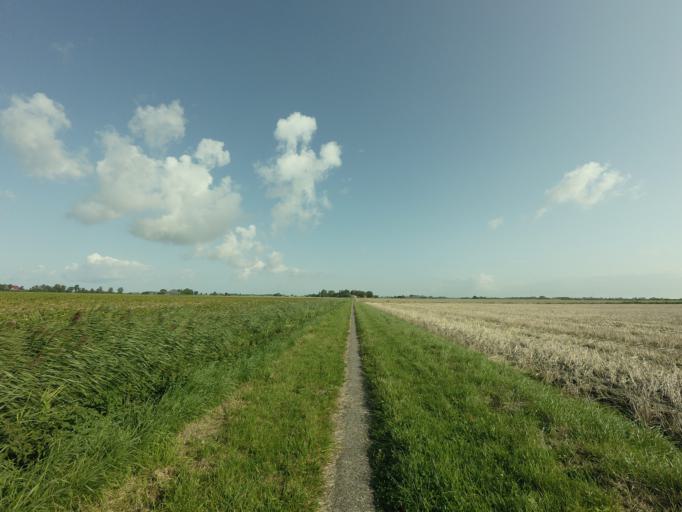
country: NL
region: Friesland
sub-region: Gemeente Franekeradeel
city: Franeker
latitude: 53.2044
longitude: 5.5645
